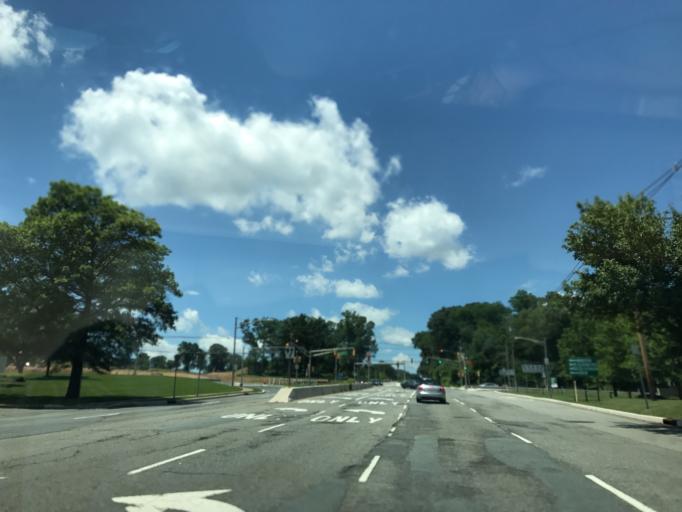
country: US
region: New Jersey
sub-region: Morris County
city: Madison
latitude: 40.7930
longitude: -74.4331
